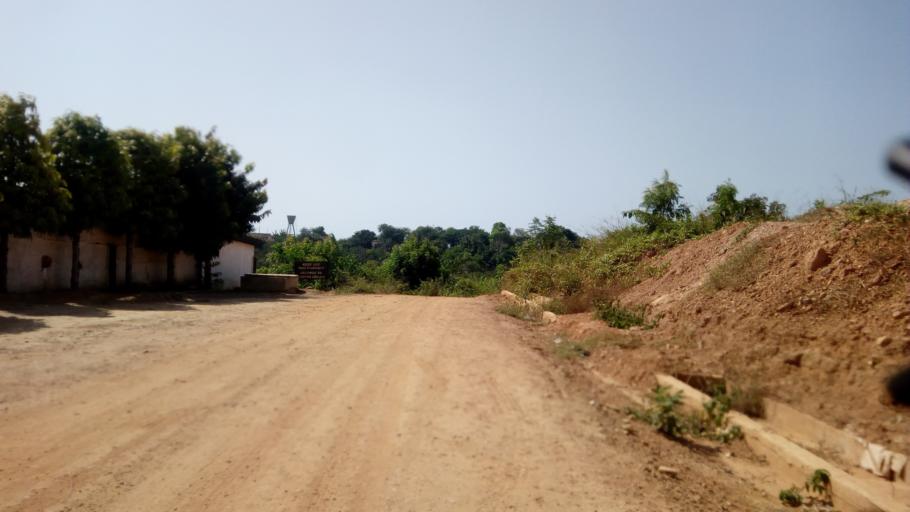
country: GH
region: Central
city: Cape Coast
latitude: 5.1107
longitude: -1.2677
